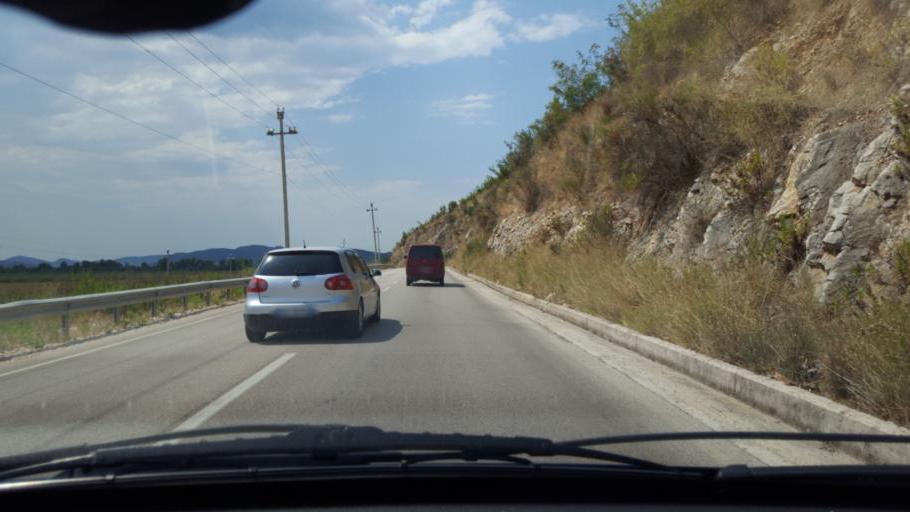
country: AL
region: Vlore
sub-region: Rrethi i Sarandes
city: Sarande
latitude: 39.8252
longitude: 20.0215
